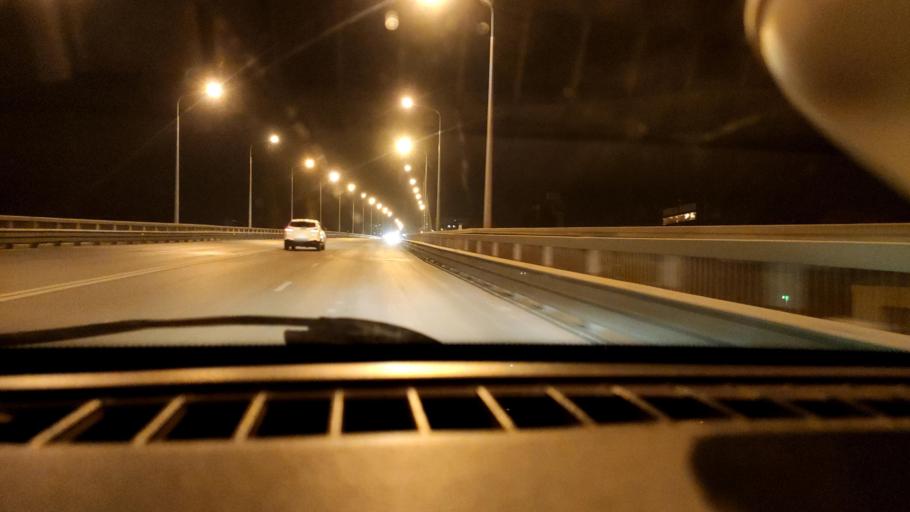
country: RU
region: Samara
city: Samara
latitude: 53.1733
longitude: 50.1943
